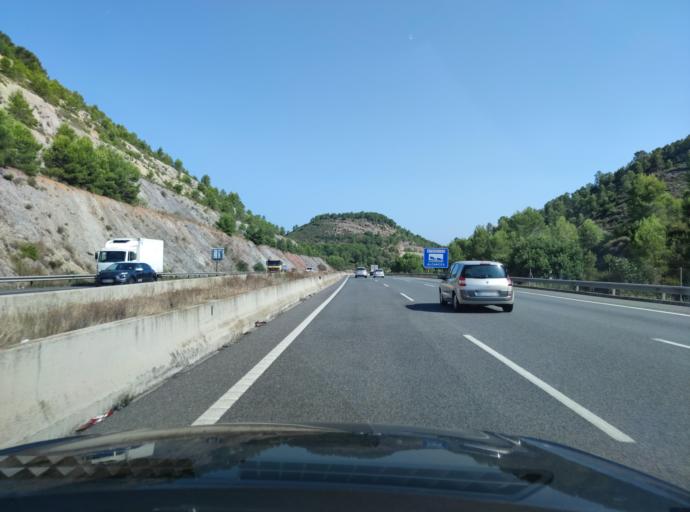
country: ES
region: Valencia
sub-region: Provincia de Valencia
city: Llosa de Ranes
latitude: 39.0358
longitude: -0.5518
